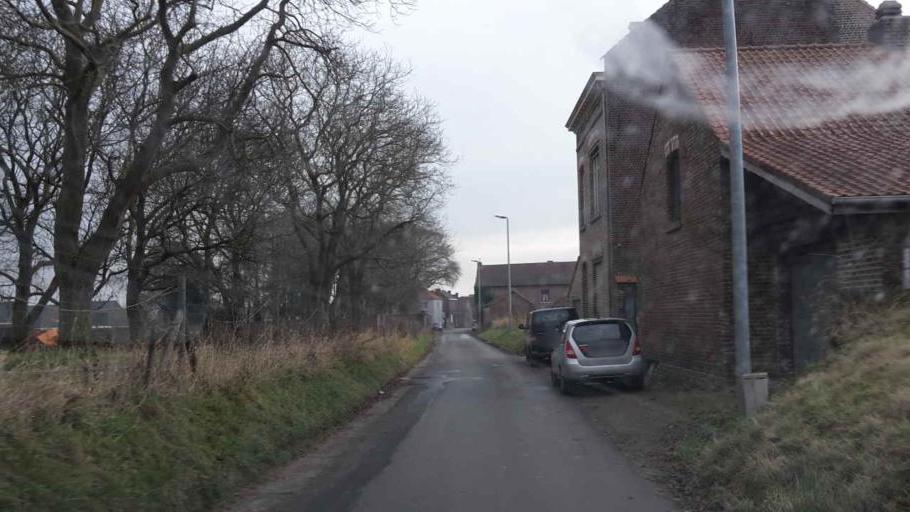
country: BE
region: Flanders
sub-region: Provincie Vlaams-Brabant
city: Hoegaarden
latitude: 50.8168
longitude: 4.8791
